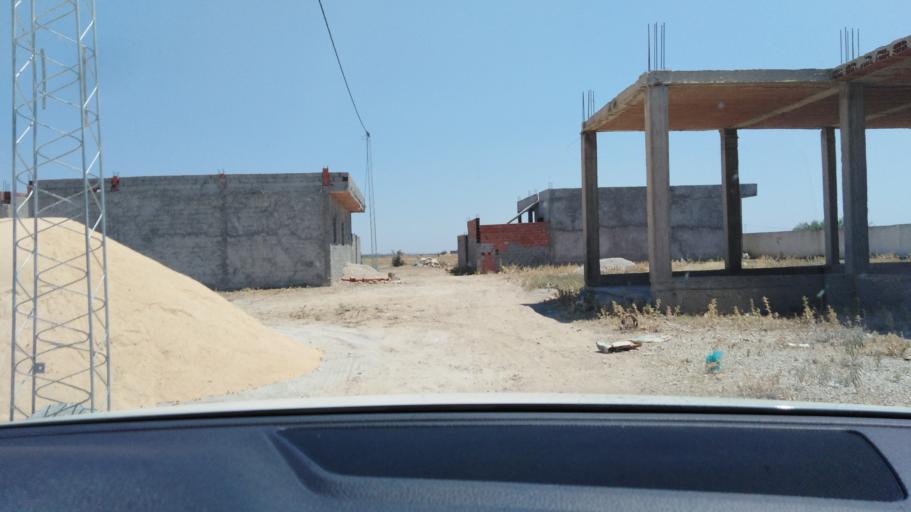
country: TN
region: Al Qayrawan
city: Sbikha
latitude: 36.1153
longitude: 10.1011
